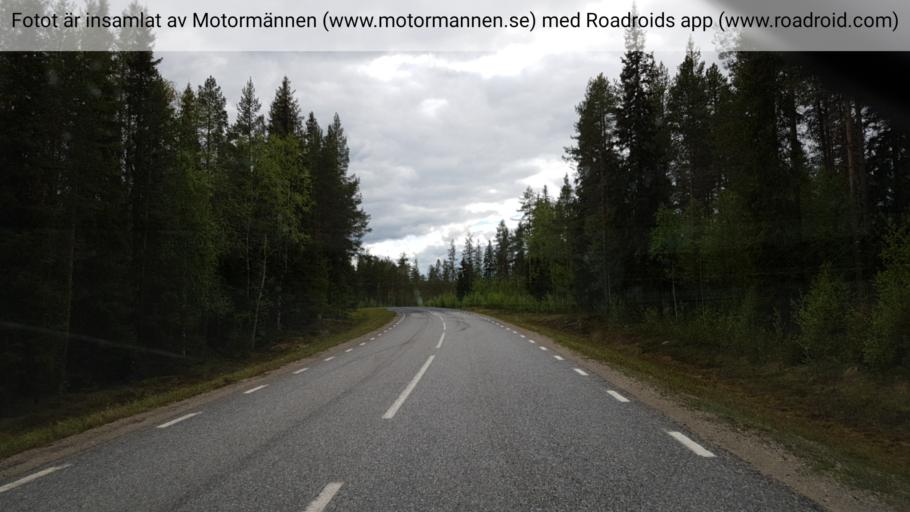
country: SE
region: Vaesterbotten
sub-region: Skelleftea Kommun
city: Langsele
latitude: 64.6037
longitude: 19.9328
